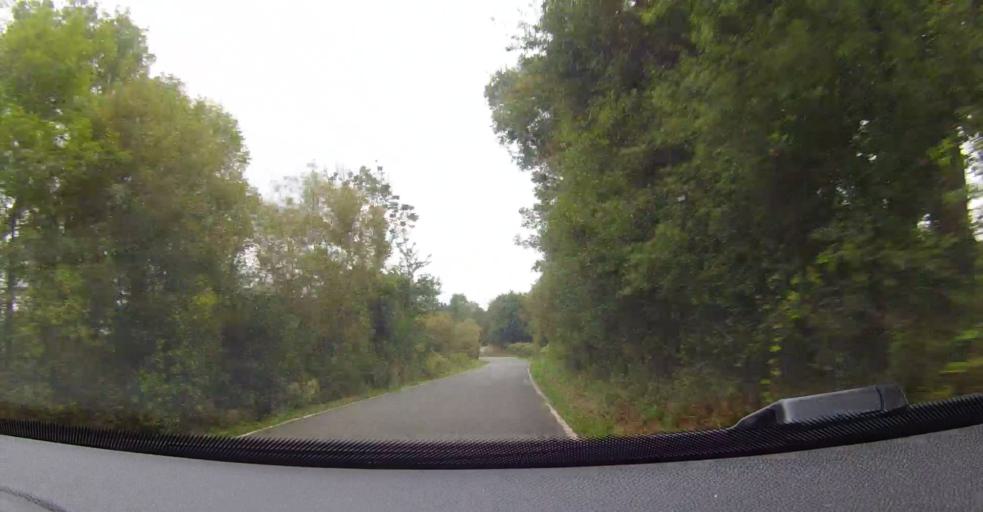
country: ES
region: Basque Country
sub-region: Bizkaia
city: Urrestieta
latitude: 43.2319
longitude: -3.1884
